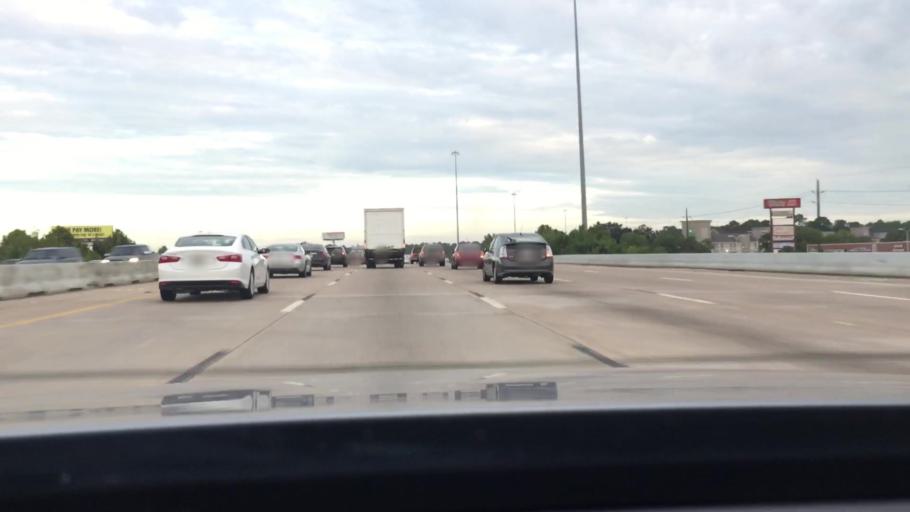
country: US
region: Texas
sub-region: Harris County
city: Jersey Village
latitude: 29.9671
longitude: -95.5565
